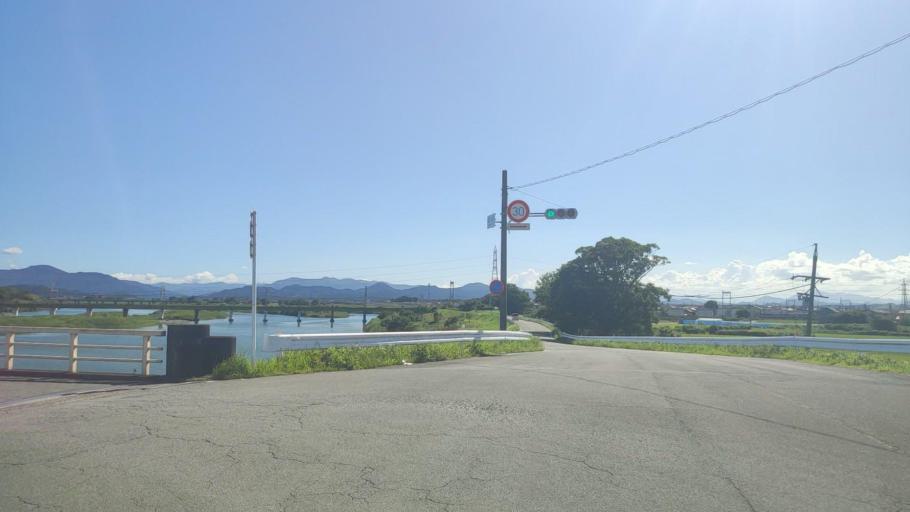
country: JP
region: Mie
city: Ise
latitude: 34.5131
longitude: 136.6914
